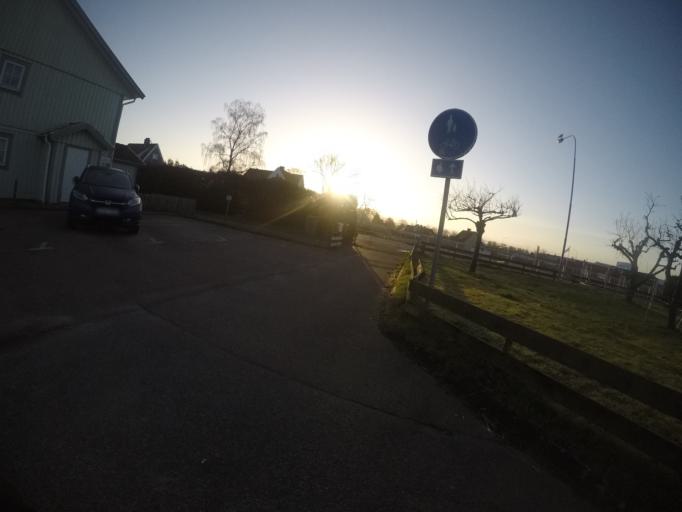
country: SE
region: Halland
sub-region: Laholms Kommun
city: Laholm
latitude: 56.5055
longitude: 13.0344
